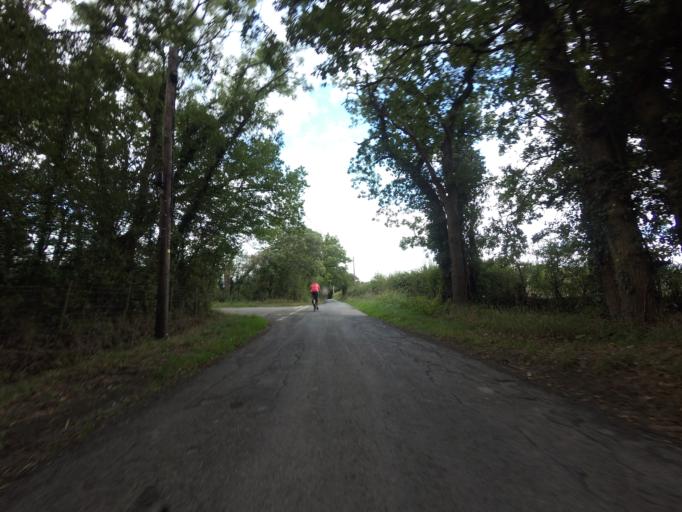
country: GB
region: England
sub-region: Kent
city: Staplehurst
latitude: 51.2102
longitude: 0.5446
